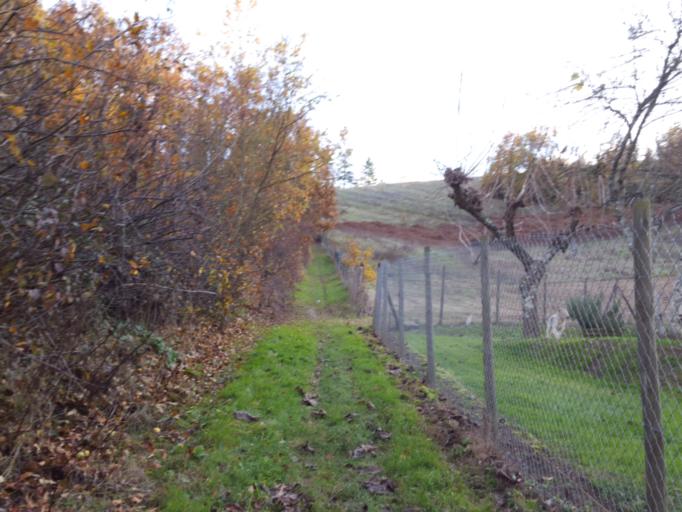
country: FR
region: Midi-Pyrenees
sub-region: Departement du Tarn-et-Garonne
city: Moissac
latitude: 44.1124
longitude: 1.0989
